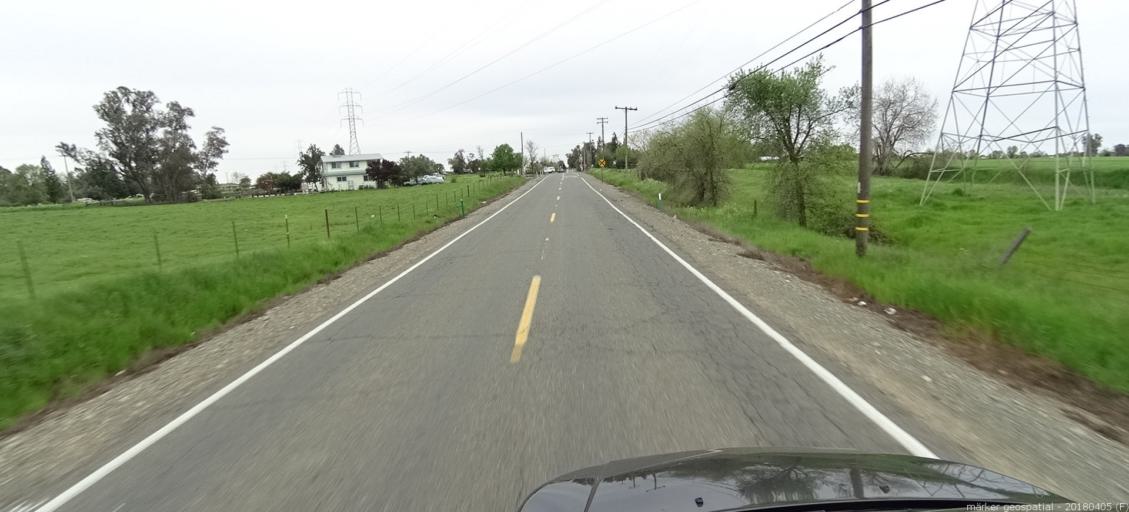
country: US
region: California
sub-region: Sacramento County
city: Herald
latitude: 38.3076
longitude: -121.2264
